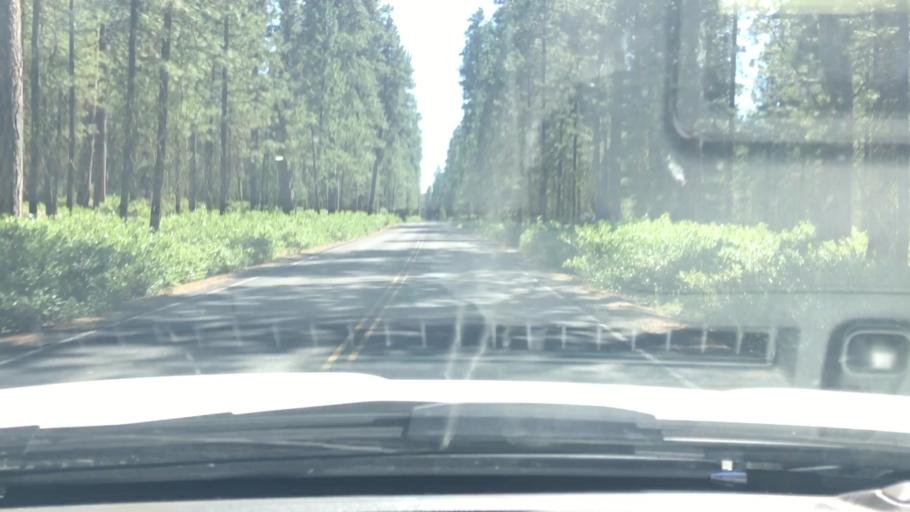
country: US
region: Oregon
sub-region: Deschutes County
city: Sisters
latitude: 44.4224
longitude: -121.6676
